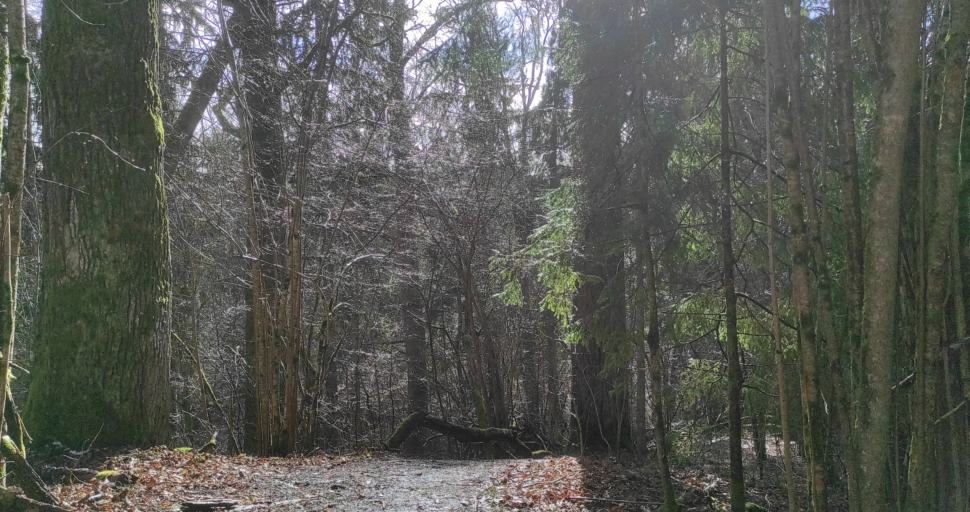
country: LV
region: Tukuma Rajons
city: Tukums
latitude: 57.1167
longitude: 23.0394
